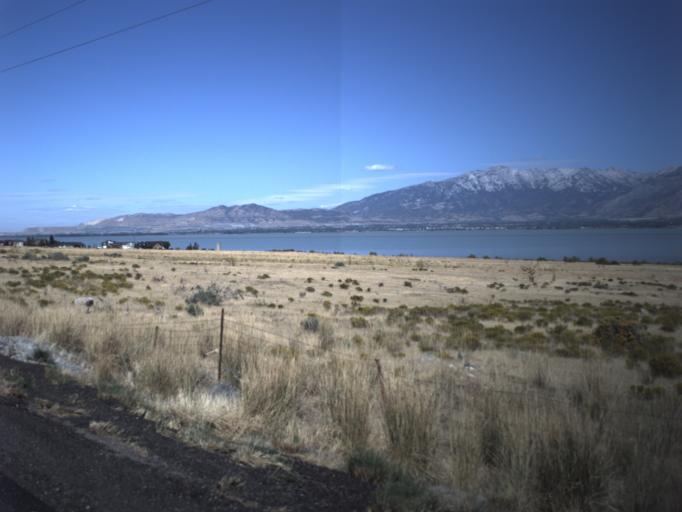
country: US
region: Utah
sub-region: Utah County
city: Saratoga Springs
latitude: 40.2761
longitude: -111.8677
